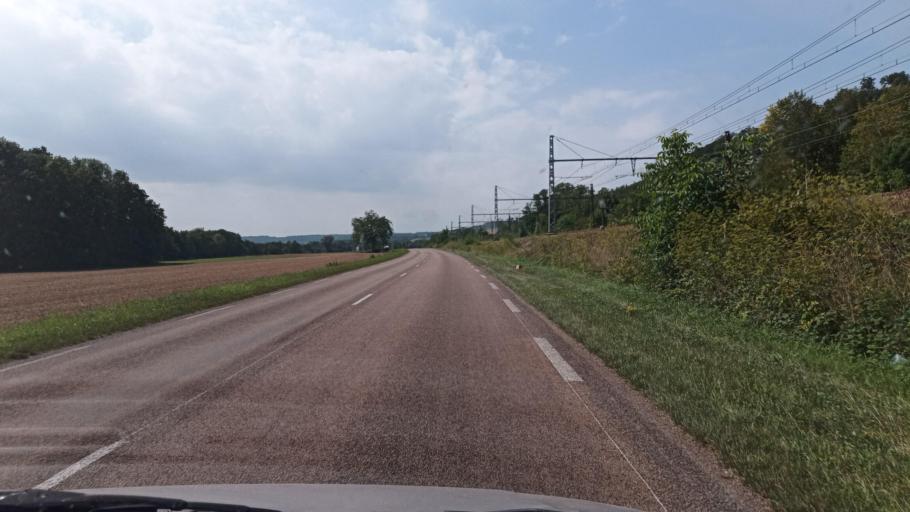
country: FR
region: Bourgogne
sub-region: Departement de l'Yonne
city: Veron
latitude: 48.1244
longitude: 3.2784
